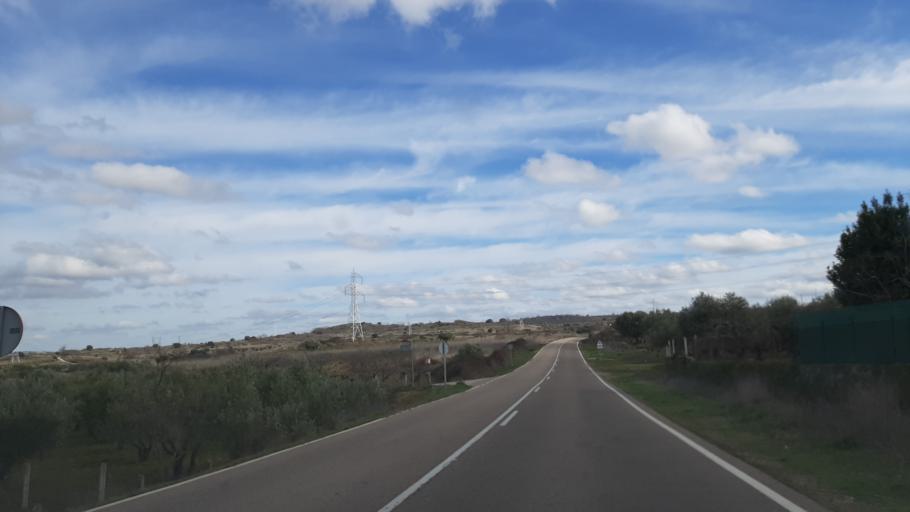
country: ES
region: Castille and Leon
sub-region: Provincia de Salamanca
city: Villarino de los Aires
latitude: 41.2675
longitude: -6.4567
